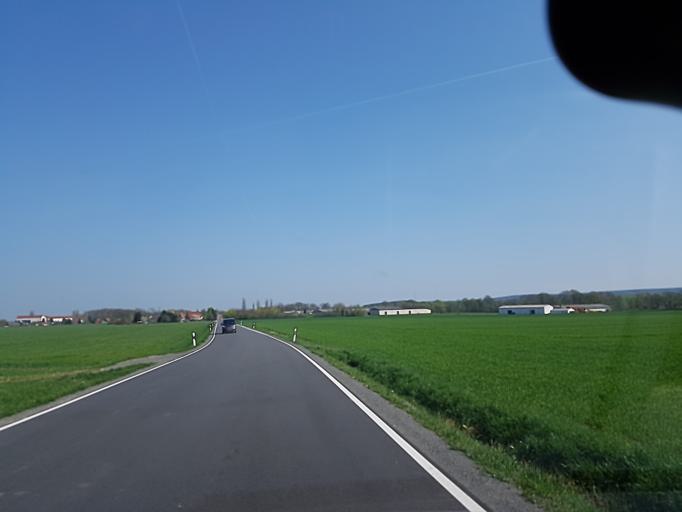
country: DE
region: Saxony
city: Cavertitz
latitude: 51.3875
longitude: 13.1129
